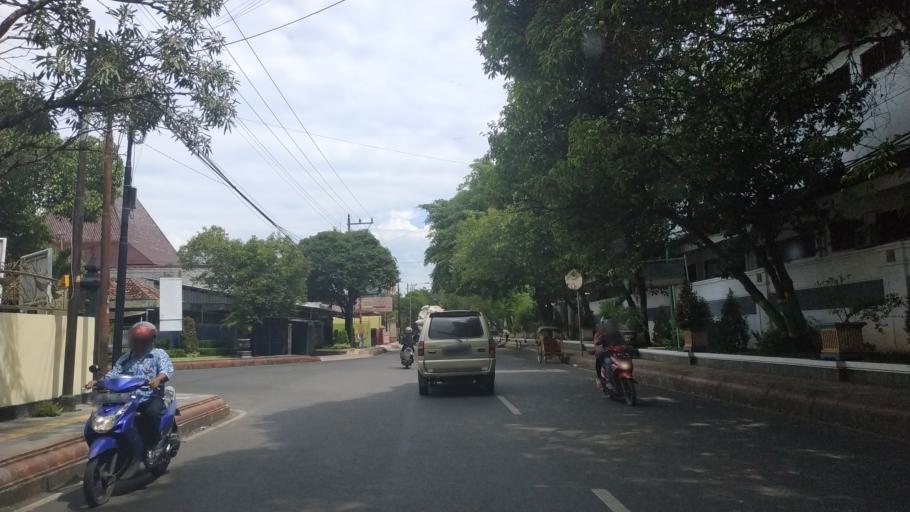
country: ID
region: Central Java
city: Pati
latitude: -6.7517
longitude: 111.0408
